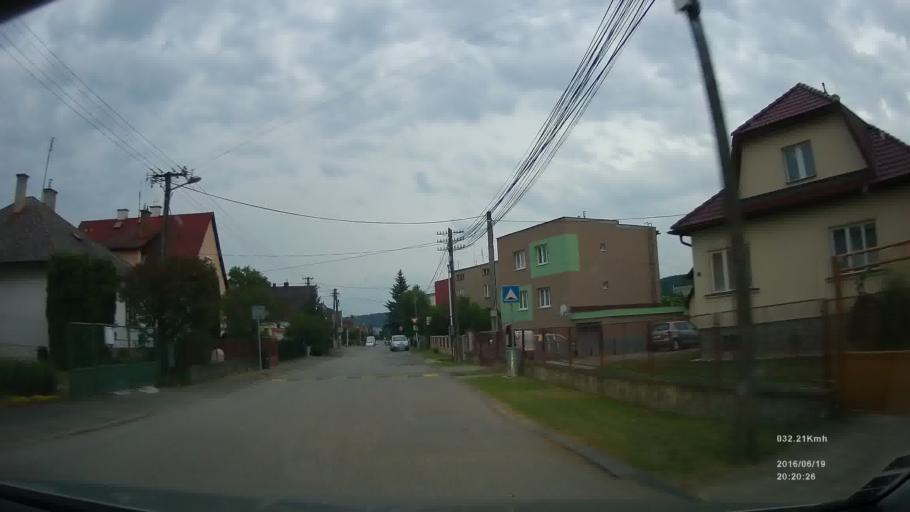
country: SK
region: Presovsky
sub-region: Okres Presov
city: Presov
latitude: 48.9743
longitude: 21.2585
